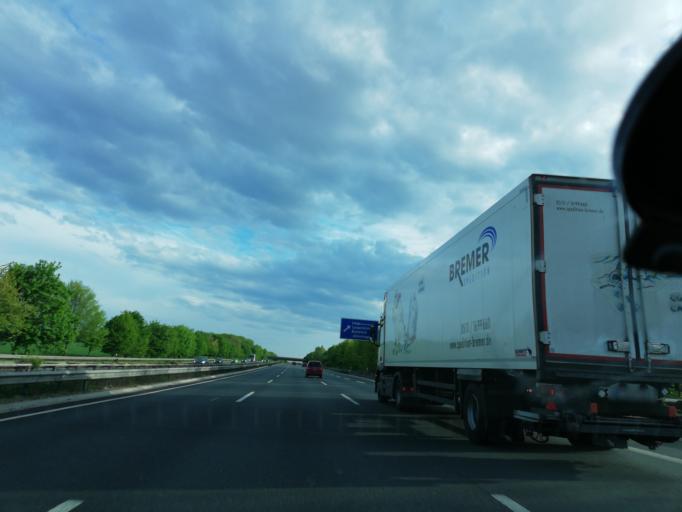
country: DE
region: North Rhine-Westphalia
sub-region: Regierungsbezirk Detmold
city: Herford
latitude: 52.0632
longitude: 8.6606
